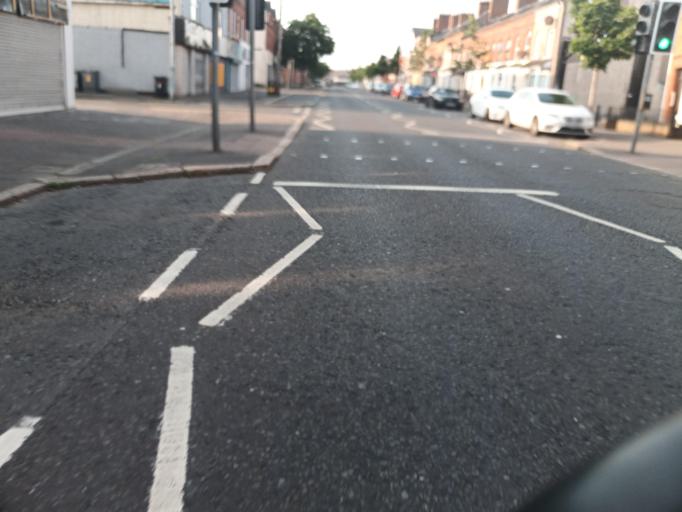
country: GB
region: Northern Ireland
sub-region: Castlereagh District
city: Castlereagh
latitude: 54.5962
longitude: -5.8887
